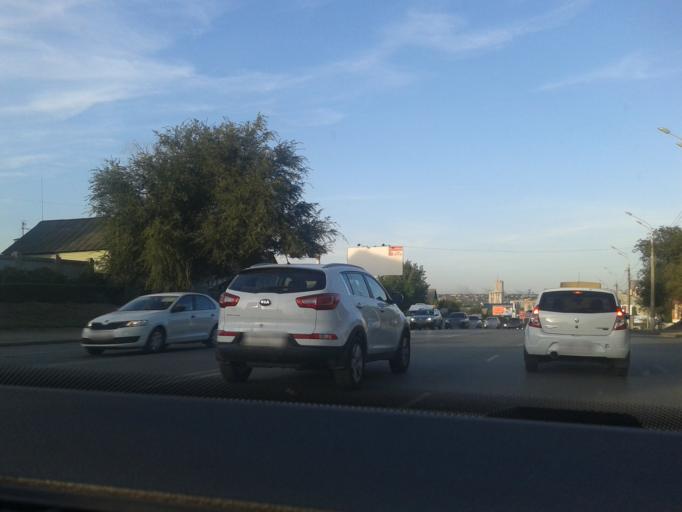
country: RU
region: Volgograd
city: Volgograd
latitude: 48.7002
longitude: 44.4755
